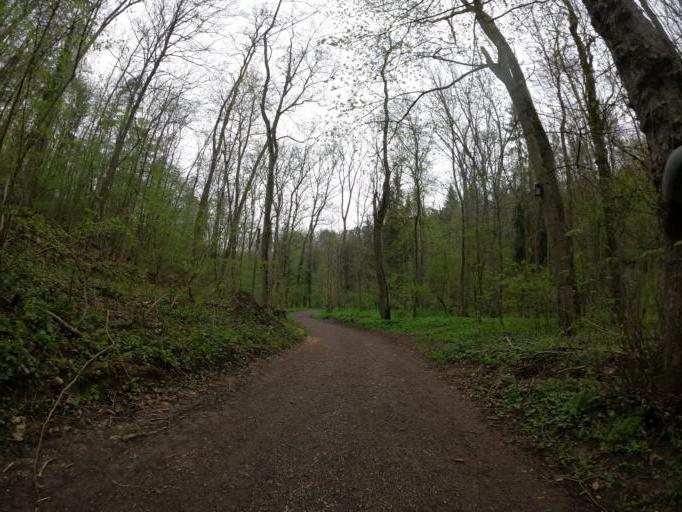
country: DE
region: Baden-Wuerttemberg
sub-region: Regierungsbezirk Stuttgart
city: Markgroningen
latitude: 48.9199
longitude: 9.0795
